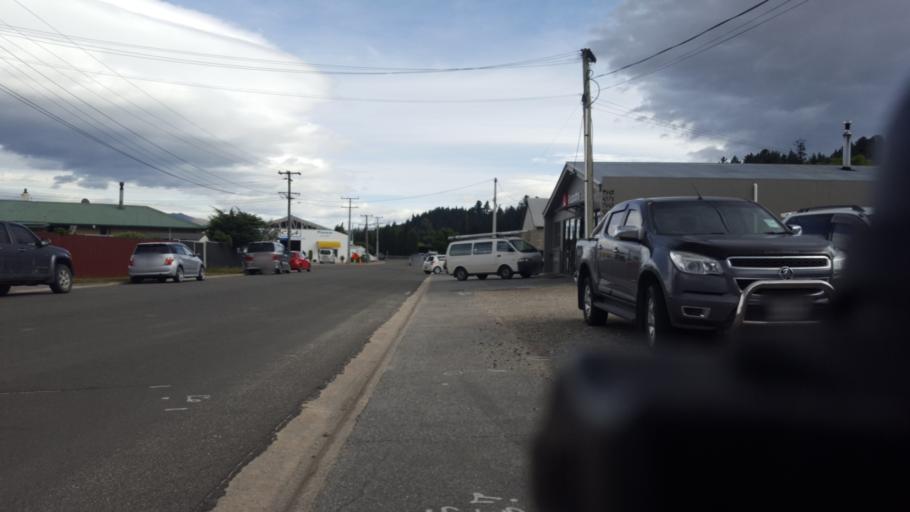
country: NZ
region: Otago
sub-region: Queenstown-Lakes District
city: Wanaka
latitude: -45.2458
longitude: 169.3969
